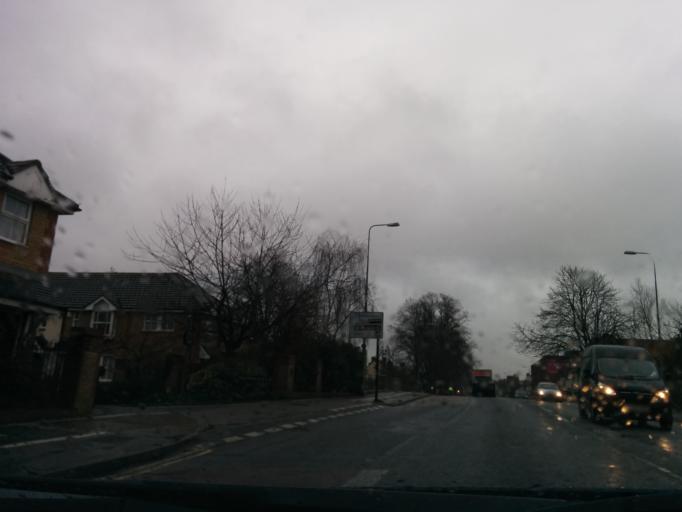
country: GB
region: England
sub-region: Oxfordshire
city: Oxford
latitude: 51.7527
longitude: -1.2821
